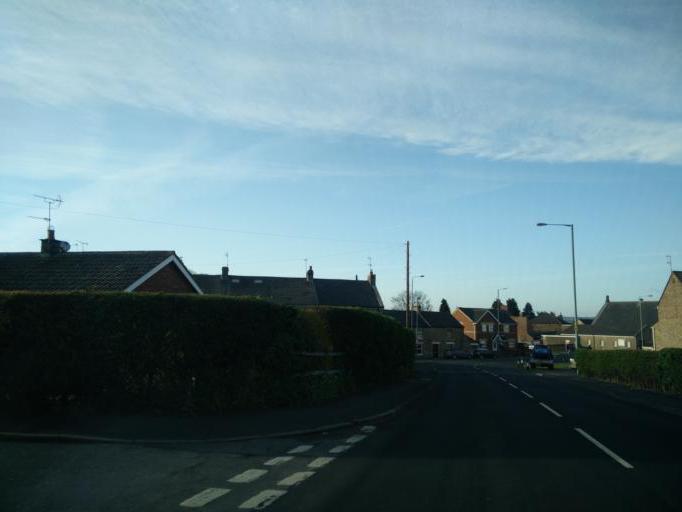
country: GB
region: England
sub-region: County Durham
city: Crook
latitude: 54.6970
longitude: -1.7478
